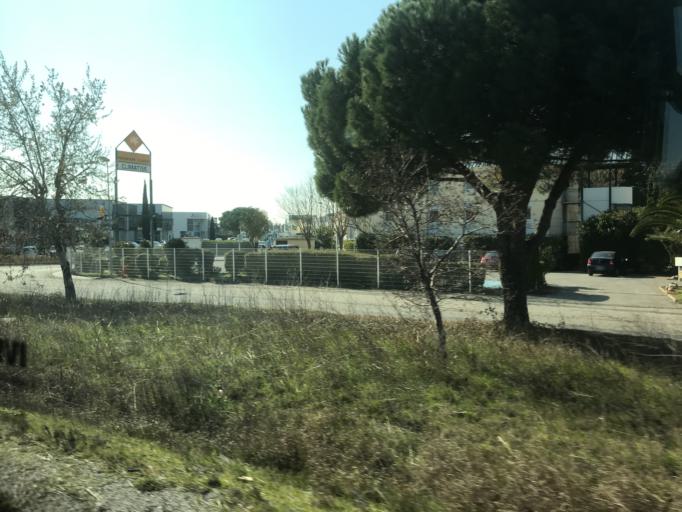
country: FR
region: Languedoc-Roussillon
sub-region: Departement de l'Herault
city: Perols
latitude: 43.5904
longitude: 3.9402
